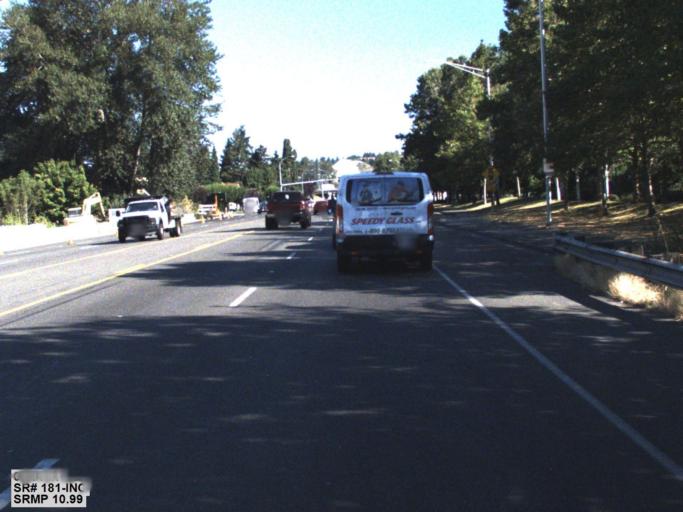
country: US
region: Washington
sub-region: King County
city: Tukwila
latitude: 47.4585
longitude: -122.2443
